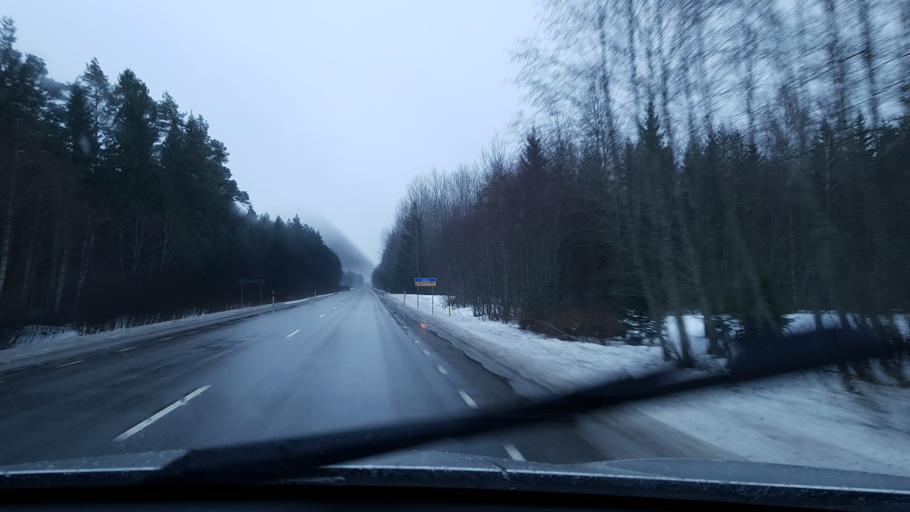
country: EE
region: Jaervamaa
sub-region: Tueri vald
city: Sarevere
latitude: 58.8084
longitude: 25.2010
